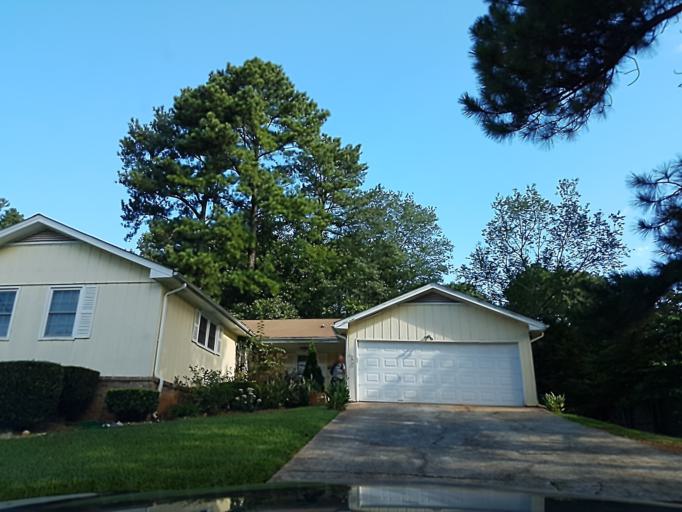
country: US
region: Georgia
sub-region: DeKalb County
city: Clarkston
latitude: 33.7841
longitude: -84.2155
